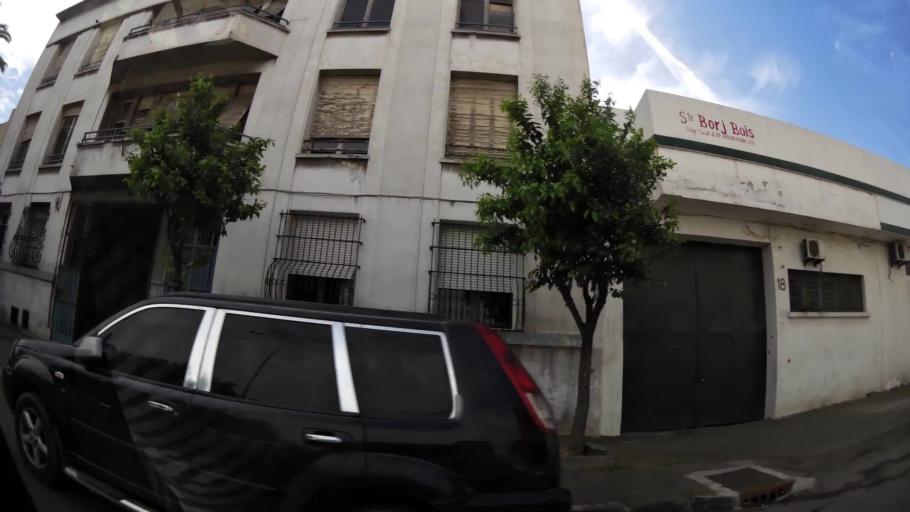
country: MA
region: Grand Casablanca
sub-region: Casablanca
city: Casablanca
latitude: 33.5818
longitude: -7.5833
